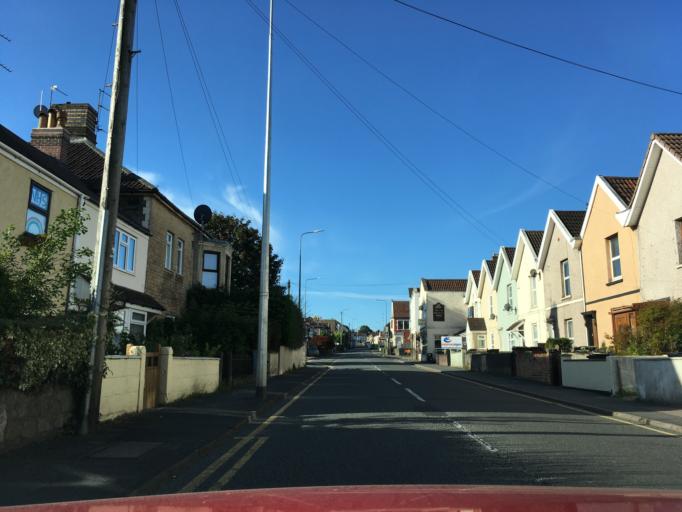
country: GB
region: England
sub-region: South Gloucestershire
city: Mangotsfield
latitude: 51.4771
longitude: -2.5079
